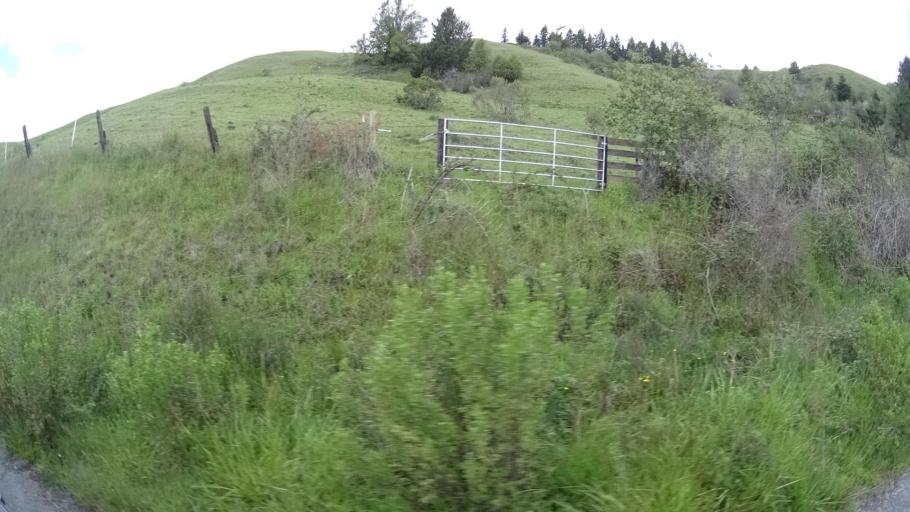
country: US
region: California
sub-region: Humboldt County
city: Blue Lake
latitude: 40.8584
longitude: -123.9294
